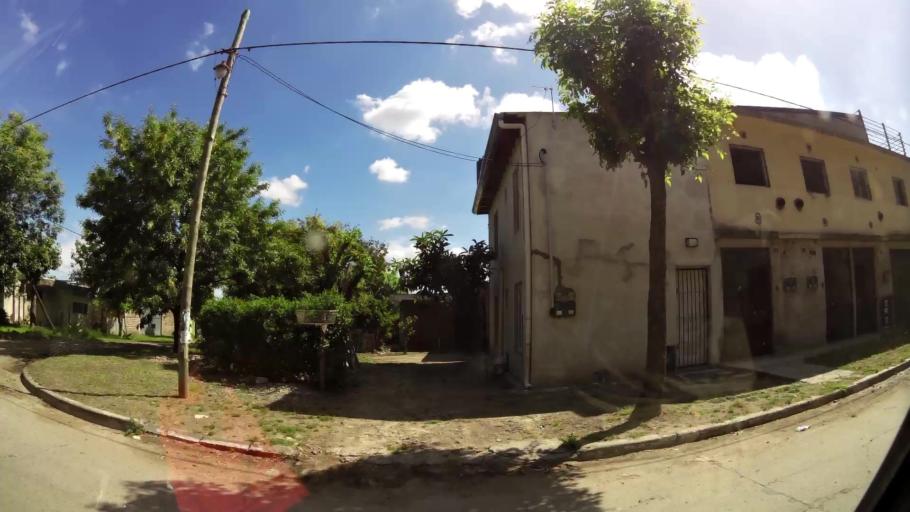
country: AR
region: Buenos Aires
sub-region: Partido de Quilmes
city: Quilmes
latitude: -34.8209
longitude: -58.2633
